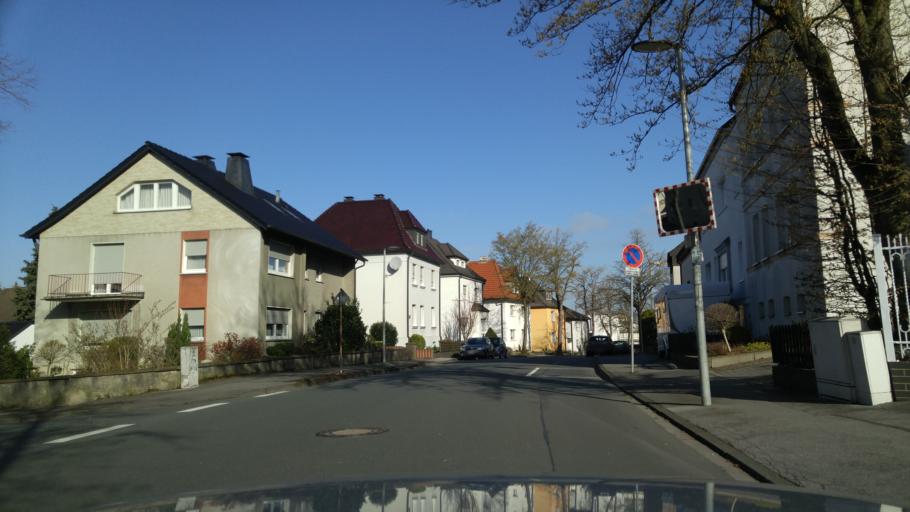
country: DE
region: North Rhine-Westphalia
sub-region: Regierungsbezirk Arnsberg
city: Menden
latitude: 51.4447
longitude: 7.7942
